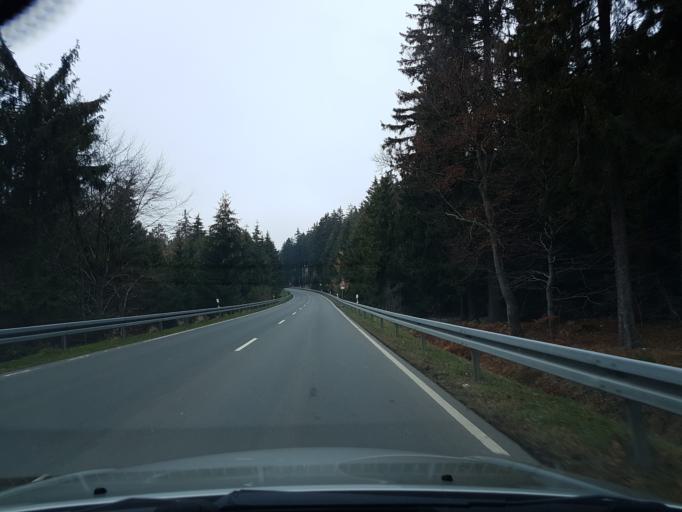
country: DE
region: Hesse
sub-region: Regierungsbezirk Darmstadt
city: Schlangenbad
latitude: 50.1071
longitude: 8.1285
